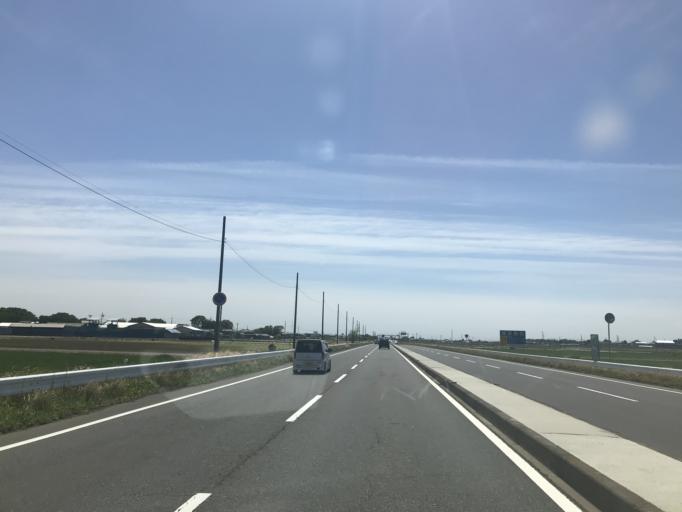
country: JP
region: Ibaraki
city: Shimodate
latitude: 36.2125
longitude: 139.9855
